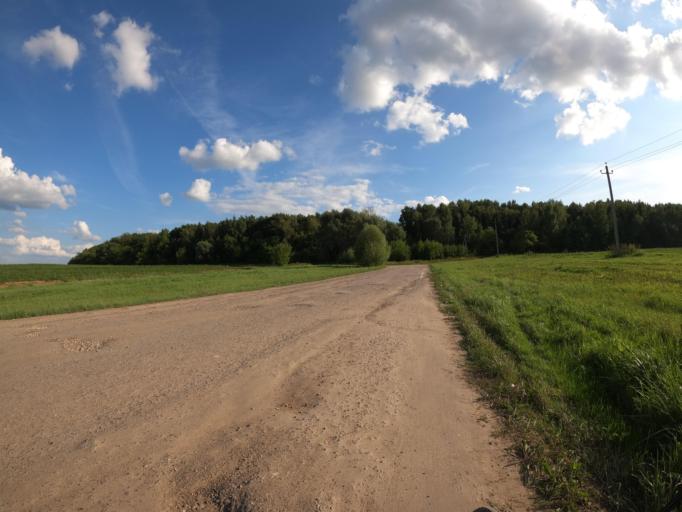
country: RU
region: Moskovskaya
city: Meshcherino
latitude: 55.1826
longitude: 38.4711
